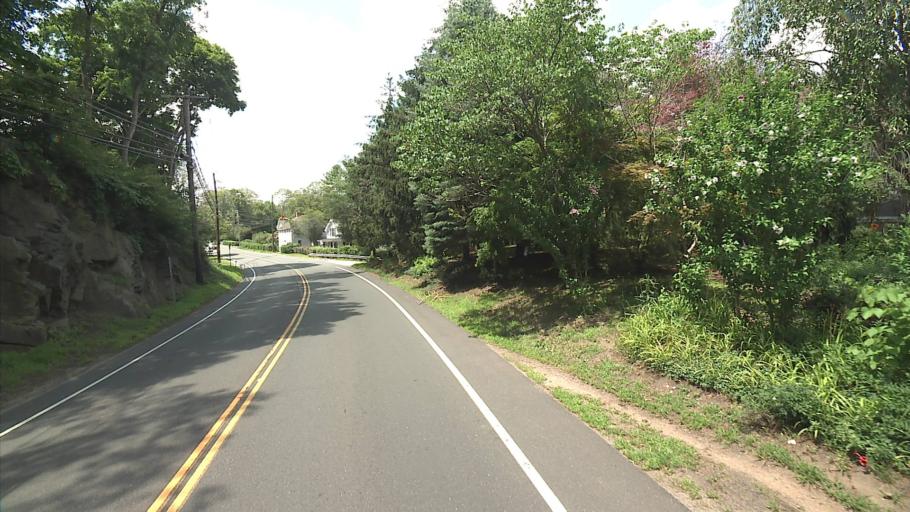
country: US
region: Connecticut
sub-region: Middlesex County
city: Higganum
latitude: 41.4980
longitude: -72.5502
